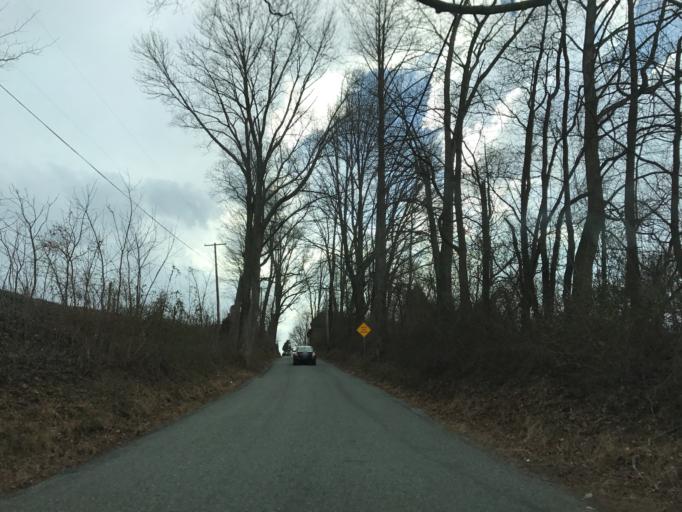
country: US
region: Maryland
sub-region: Harford County
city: South Bel Air
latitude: 39.5843
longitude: -76.3004
